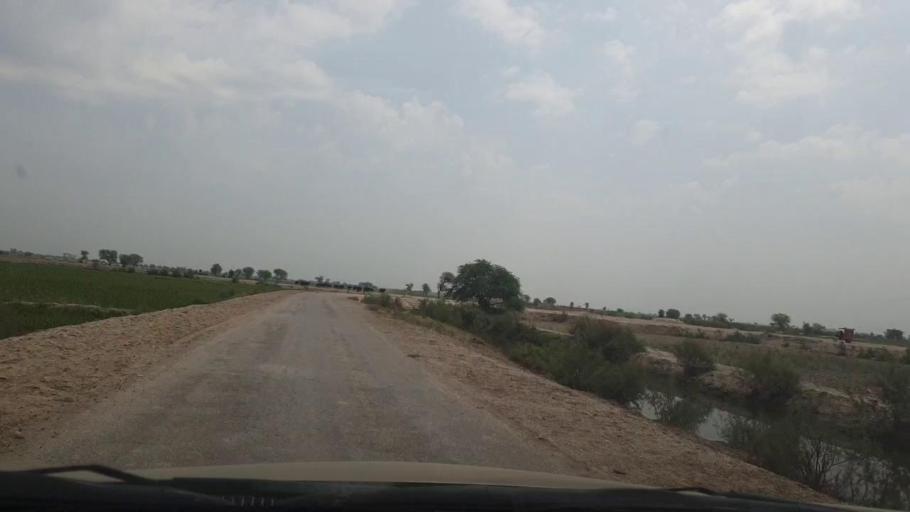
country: PK
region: Sindh
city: Ratodero
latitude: 27.7092
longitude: 68.2732
